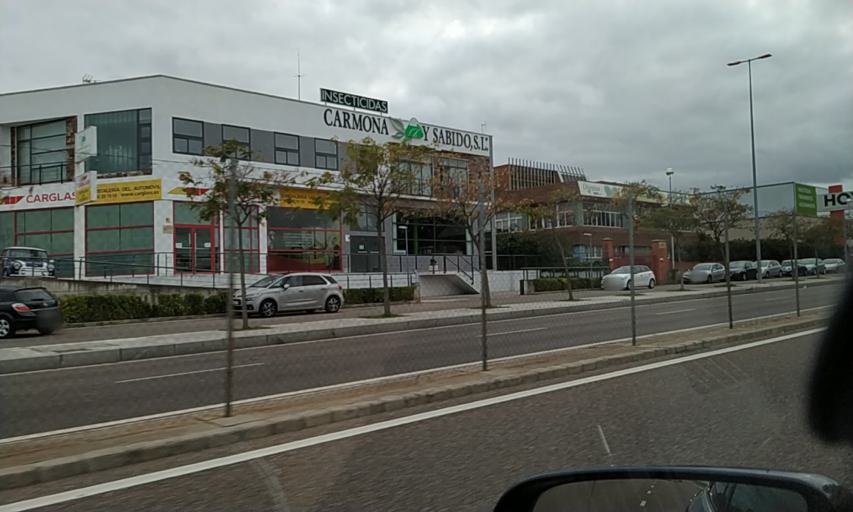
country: ES
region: Extremadura
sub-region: Provincia de Badajoz
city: Badajoz
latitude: 38.8766
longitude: -6.9503
